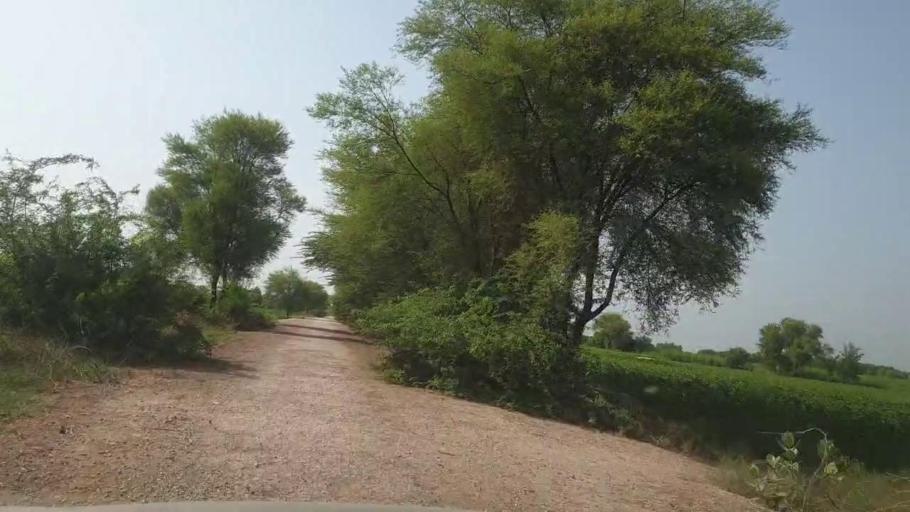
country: PK
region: Sindh
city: Pano Aqil
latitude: 27.7742
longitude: 69.1636
